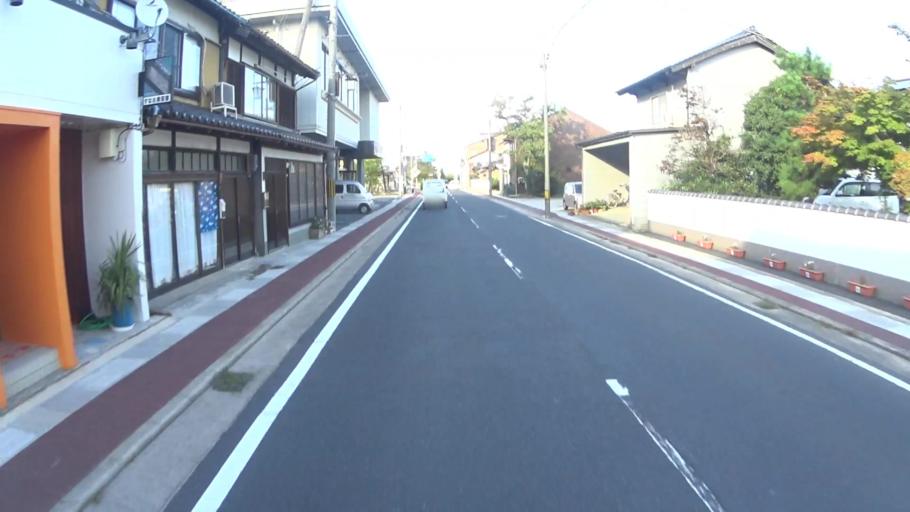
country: JP
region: Hyogo
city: Toyooka
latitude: 35.6053
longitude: 134.8959
